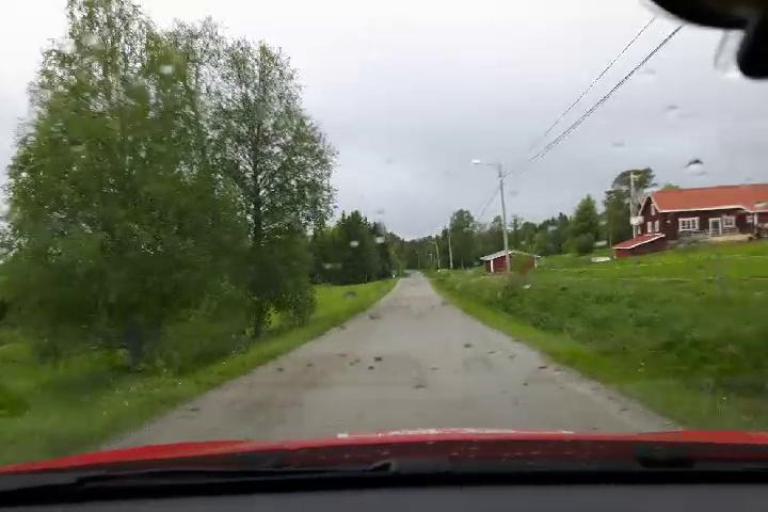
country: SE
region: Jaemtland
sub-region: Bergs Kommun
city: Hoverberg
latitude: 62.7417
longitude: 14.4568
